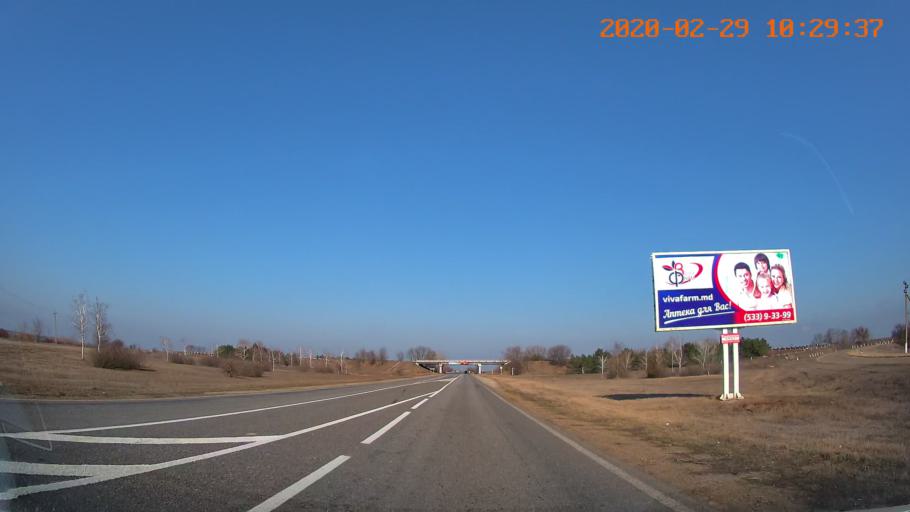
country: MD
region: Telenesti
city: Tiraspolul Nou
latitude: 46.9259
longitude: 29.5837
